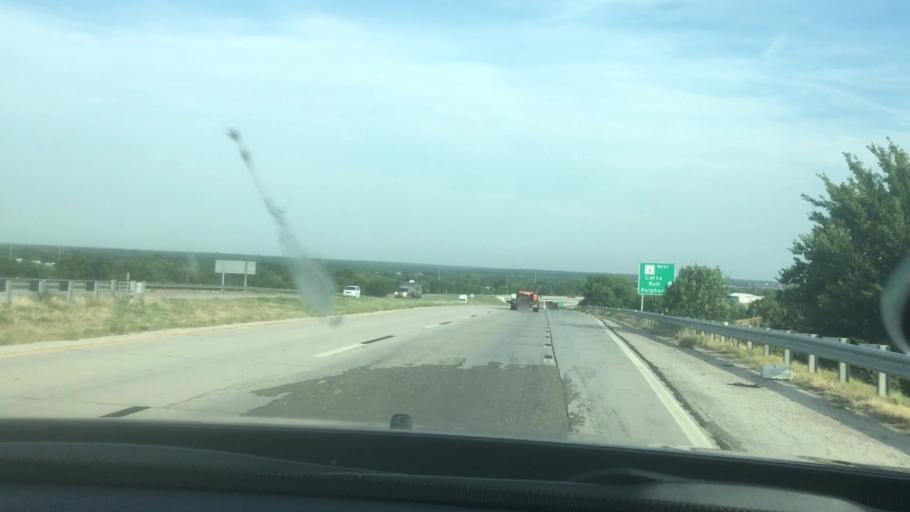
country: US
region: Oklahoma
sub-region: Pontotoc County
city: Ada
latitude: 34.7608
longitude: -96.6965
